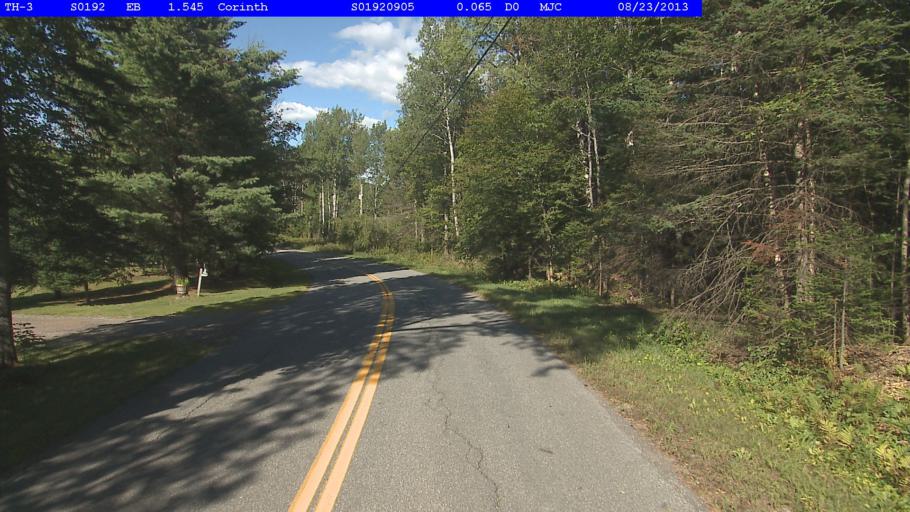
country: US
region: Vermont
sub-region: Orange County
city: Chelsea
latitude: 44.0030
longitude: -72.3518
